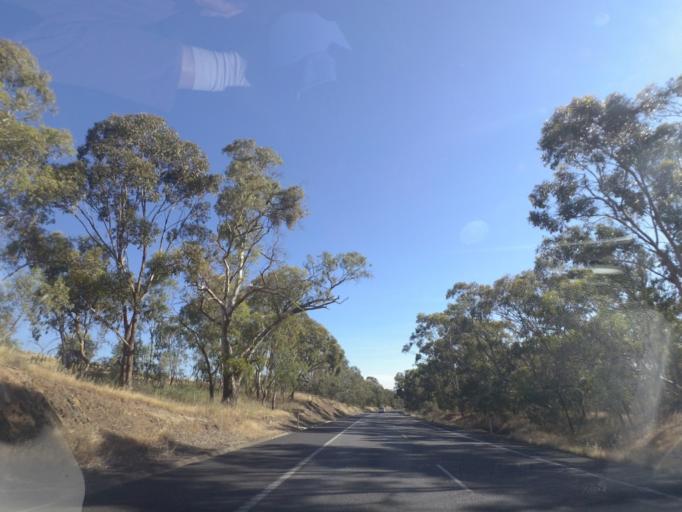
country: AU
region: Victoria
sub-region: Murrindindi
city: Kinglake West
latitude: -37.1696
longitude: 145.0769
